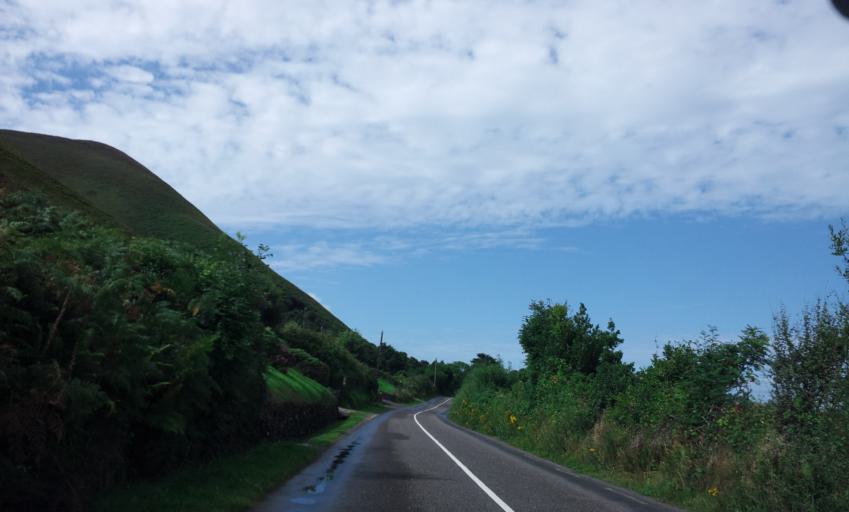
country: IE
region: Munster
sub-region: Ciarrai
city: Killorglin
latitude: 52.0558
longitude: -9.9592
